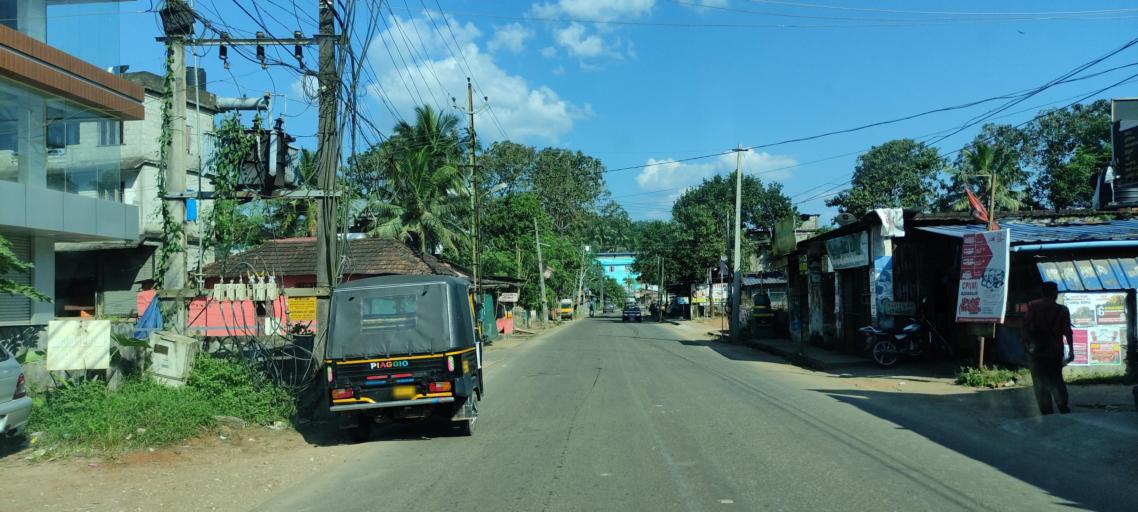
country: IN
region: Kerala
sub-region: Pattanamtitta
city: Pathanamthitta
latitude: 9.2682
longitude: 76.7984
